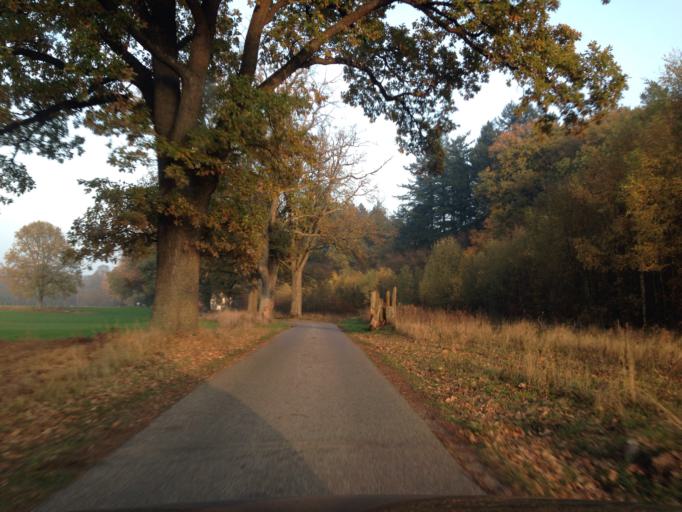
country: PL
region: Warmian-Masurian Voivodeship
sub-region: Powiat dzialdowski
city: Lidzbark
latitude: 53.2479
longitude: 19.7656
